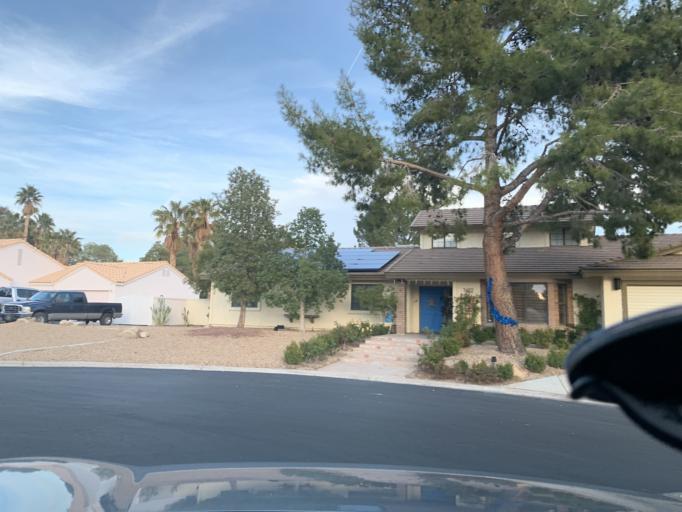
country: US
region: Nevada
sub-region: Clark County
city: Spring Valley
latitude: 36.0894
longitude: -115.2312
